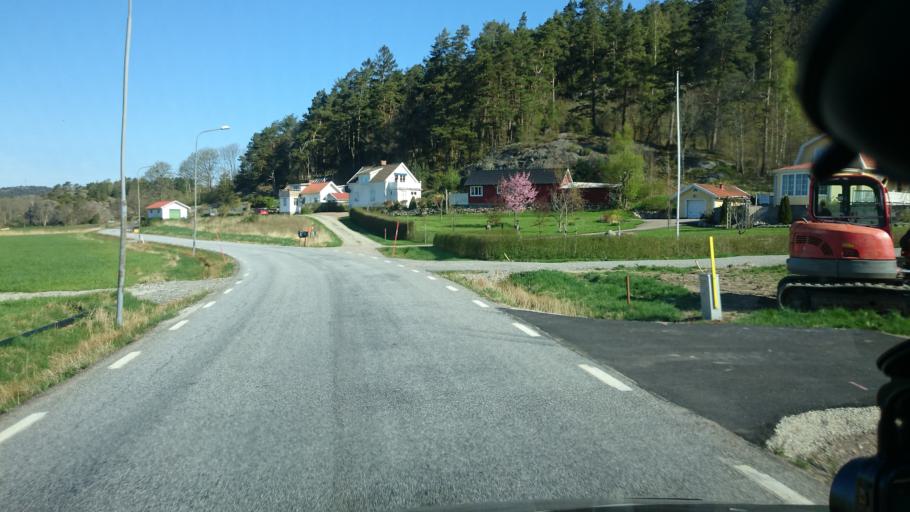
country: SE
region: Vaestra Goetaland
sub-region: Munkedals Kommun
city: Munkedal
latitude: 58.3822
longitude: 11.6657
